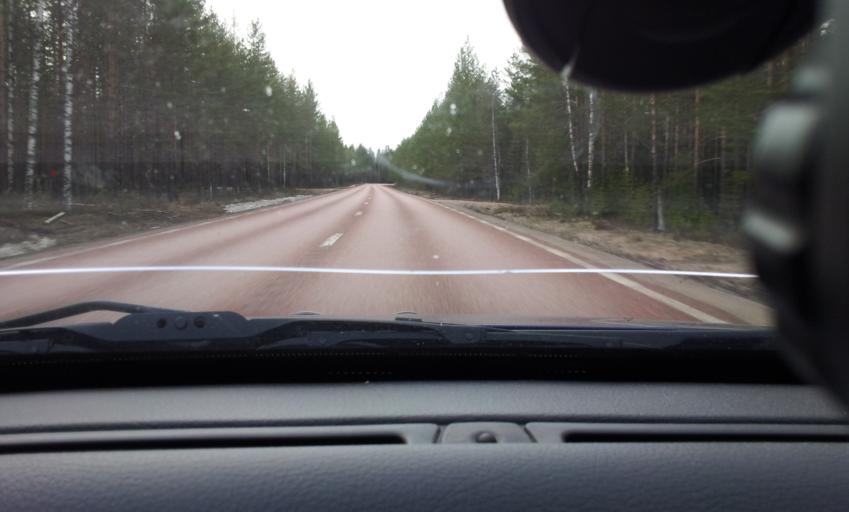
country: SE
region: Gaevleborg
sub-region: Ljusdals Kommun
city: Farila
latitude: 61.9044
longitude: 15.6370
